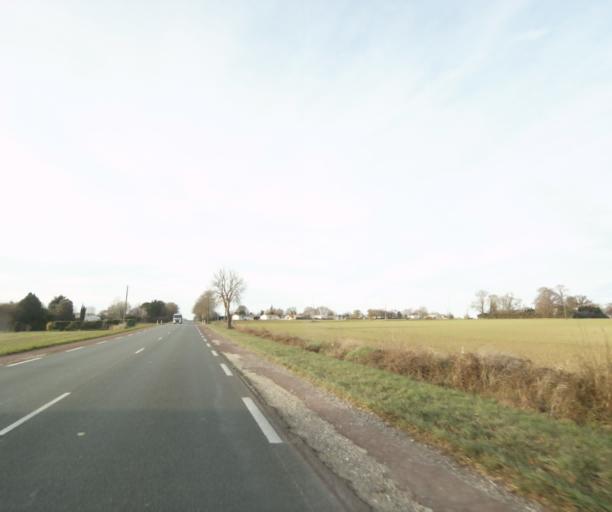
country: FR
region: Poitou-Charentes
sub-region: Departement de la Charente-Maritime
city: Saint-Georges-des-Coteaux
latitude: 45.7842
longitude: -0.7130
